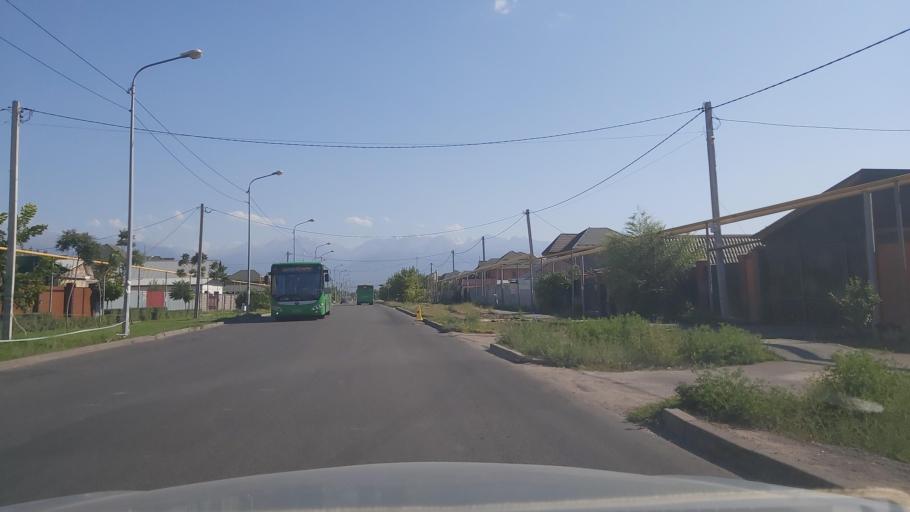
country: KZ
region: Almaty Oblysy
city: Burunday
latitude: 43.3184
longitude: 76.8416
